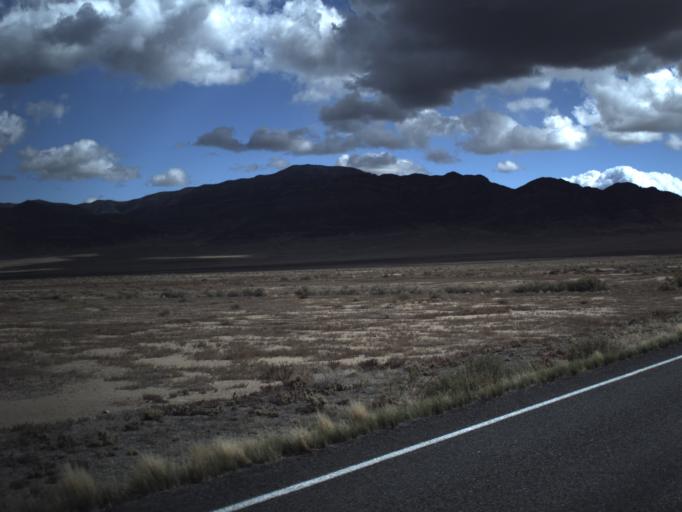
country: US
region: Utah
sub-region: Beaver County
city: Milford
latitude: 38.5259
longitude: -113.6645
